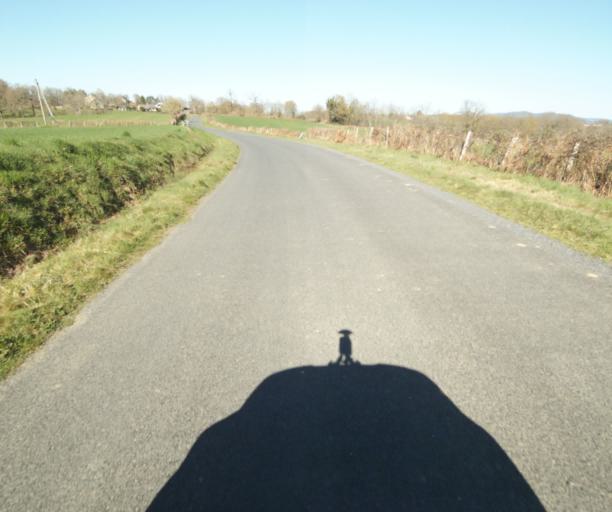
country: FR
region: Limousin
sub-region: Departement de la Correze
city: Chamboulive
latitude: 45.4356
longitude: 1.6714
